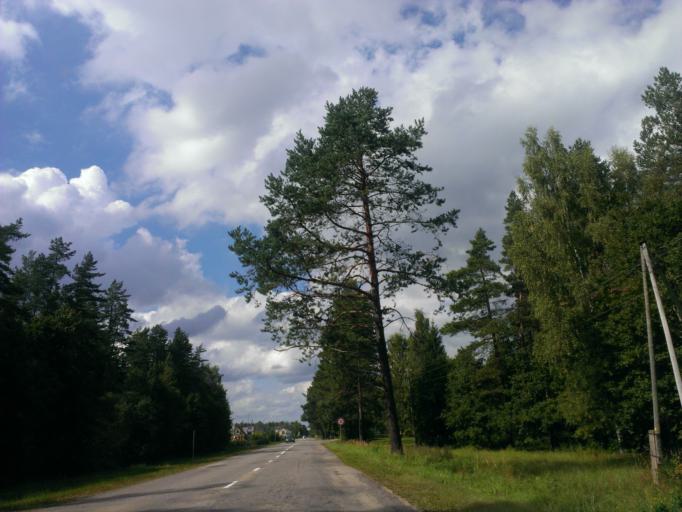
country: LV
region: Garkalne
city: Garkalne
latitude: 56.9671
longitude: 24.4876
